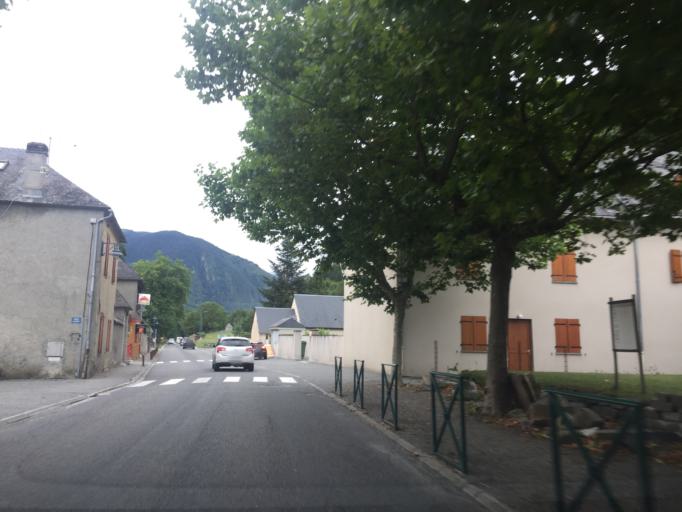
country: FR
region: Midi-Pyrenees
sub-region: Departement des Hautes-Pyrenees
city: Saint-Lary-Soulan
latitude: 42.8618
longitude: 0.3388
